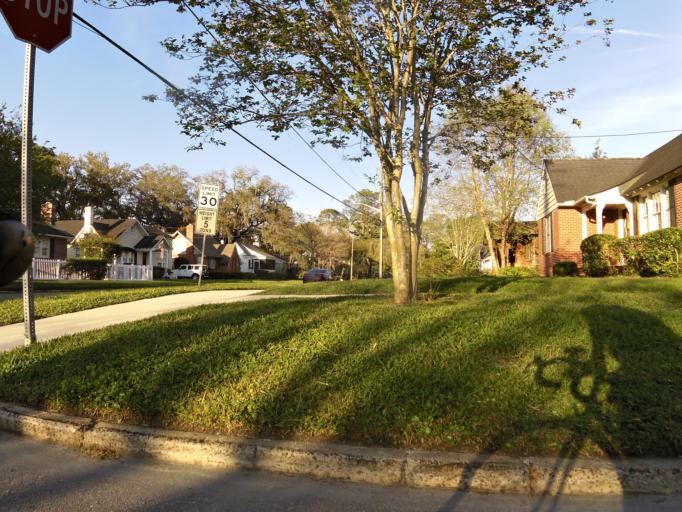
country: US
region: Florida
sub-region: Duval County
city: Jacksonville
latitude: 30.2986
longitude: -81.6475
